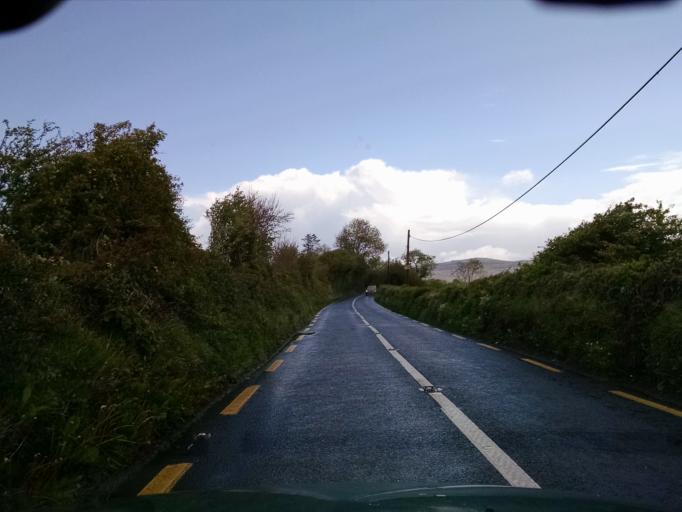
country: IE
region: Connaught
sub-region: County Galway
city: Bearna
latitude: 53.0879
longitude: -9.1760
